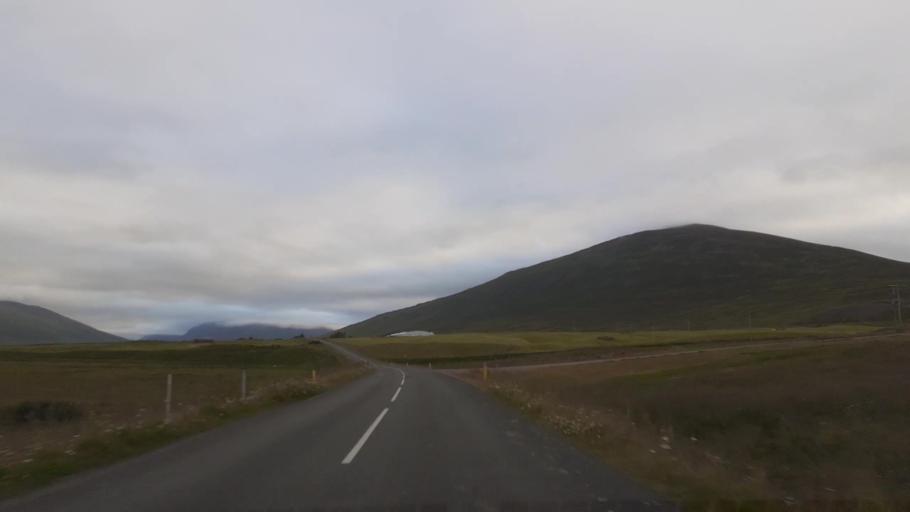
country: IS
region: Northeast
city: Dalvik
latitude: 65.9587
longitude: -18.5464
